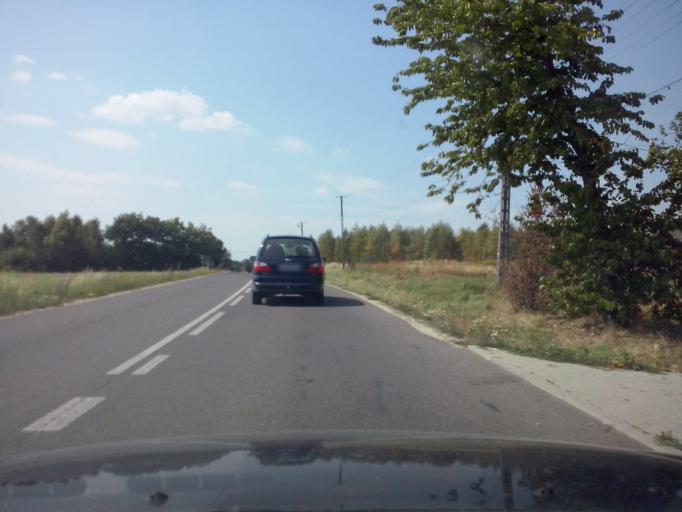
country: PL
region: Swietokrzyskie
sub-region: Powiat buski
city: Gnojno
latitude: 50.6073
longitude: 20.8131
